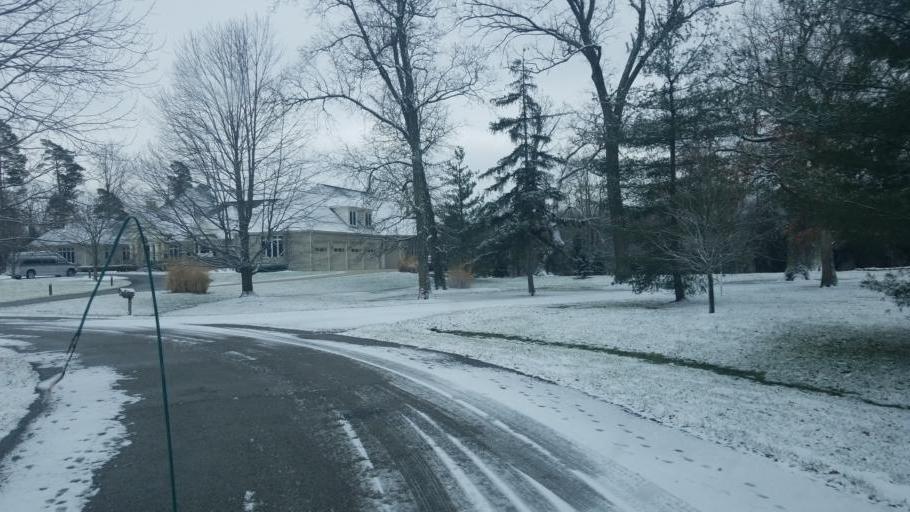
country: US
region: Ohio
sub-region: Franklin County
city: Gahanna
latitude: 40.0463
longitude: -82.8409
